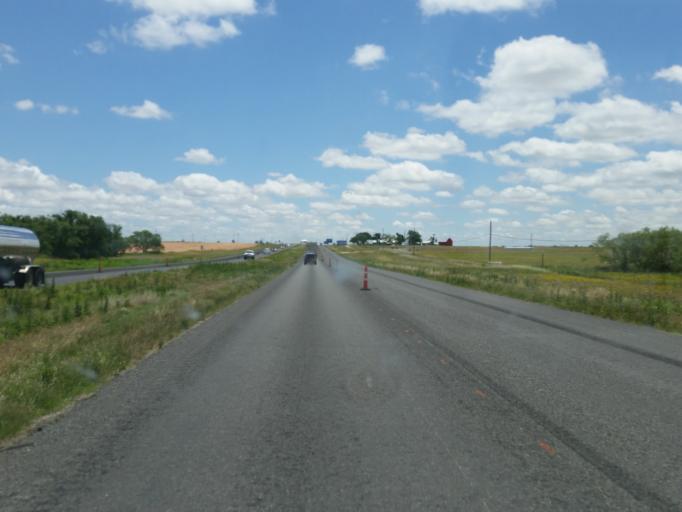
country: US
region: Texas
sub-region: Scurry County
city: Snyder
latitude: 32.7163
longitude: -100.8790
